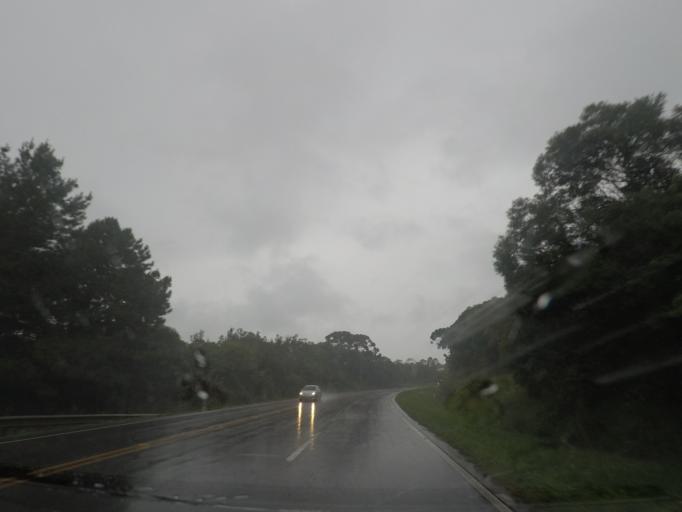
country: BR
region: Parana
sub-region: Almirante Tamandare
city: Almirante Tamandare
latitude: -25.3543
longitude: -49.3067
